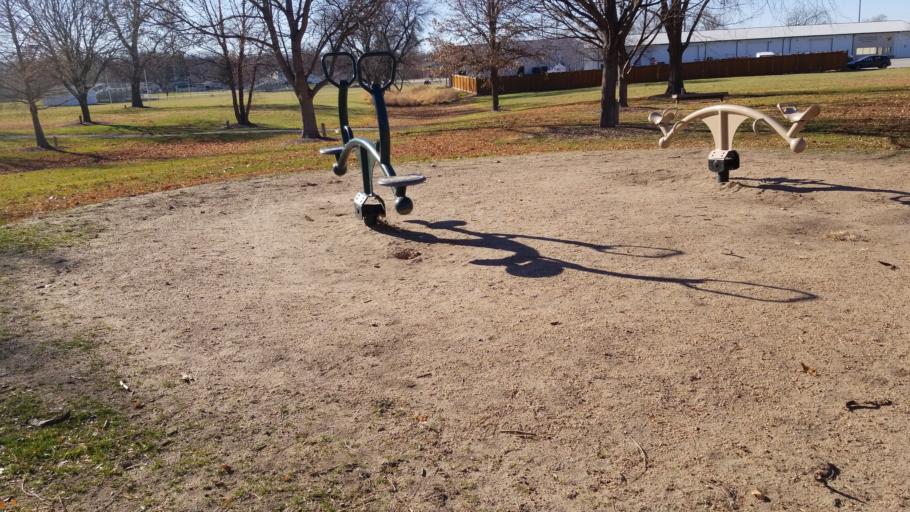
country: US
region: Nebraska
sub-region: Sarpy County
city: Papillion
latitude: 41.1540
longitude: -96.0371
